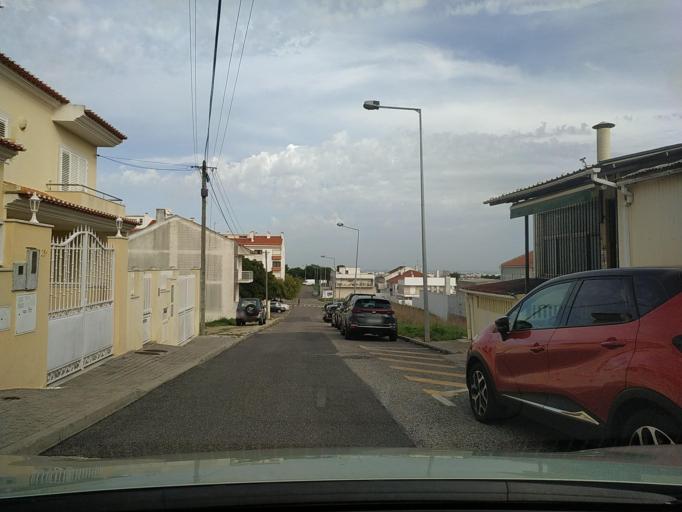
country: PT
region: Lisbon
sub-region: Amadora
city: Amadora
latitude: 38.7774
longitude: -9.2325
